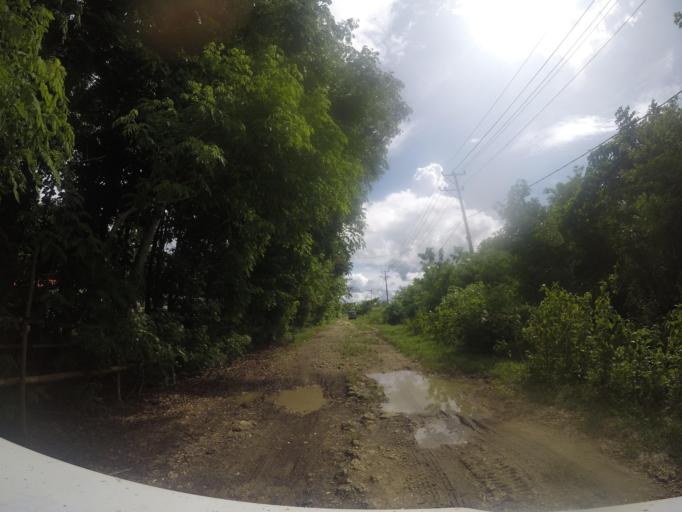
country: TL
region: Lautem
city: Lospalos
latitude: -8.4988
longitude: 127.0088
